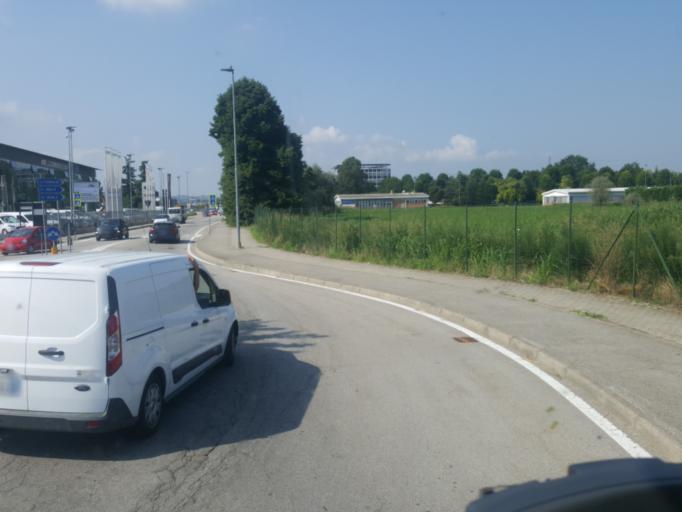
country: IT
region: Piedmont
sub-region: Provincia di Cuneo
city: Mussotto
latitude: 44.7210
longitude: 8.0373
